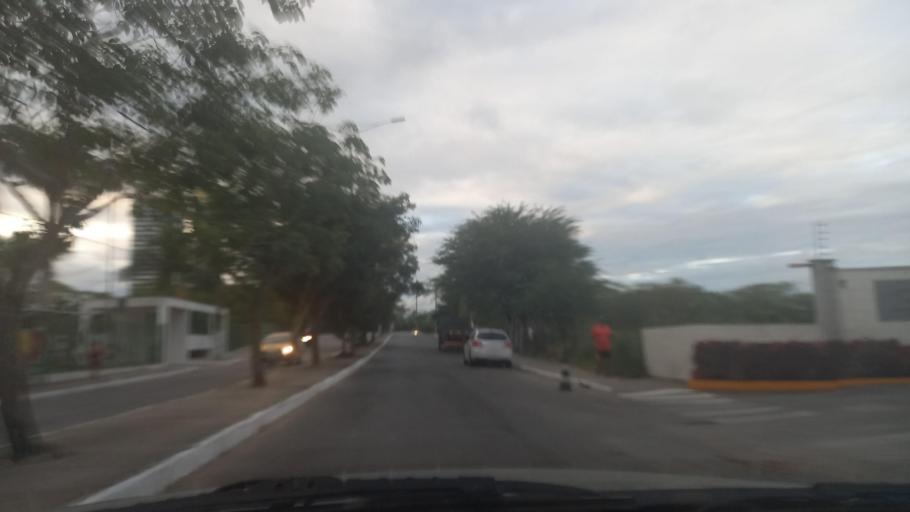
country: BR
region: Pernambuco
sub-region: Caruaru
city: Caruaru
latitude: -8.2618
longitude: -35.9646
